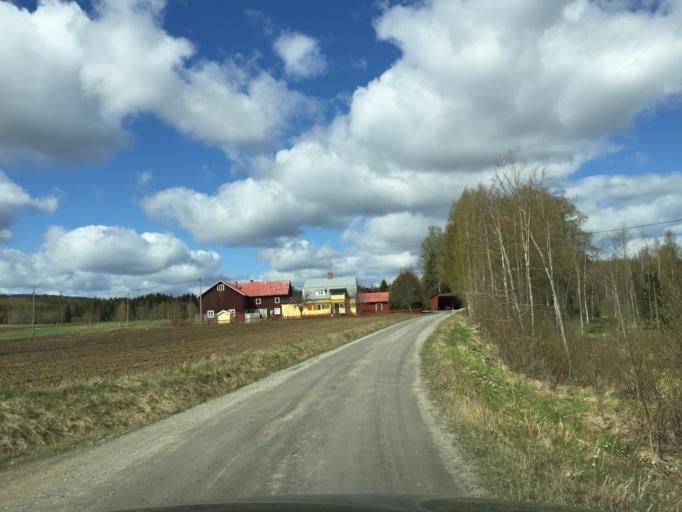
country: SE
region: Gaevleborg
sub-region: Bollnas Kommun
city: Arbra
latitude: 61.5211
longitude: 16.3345
